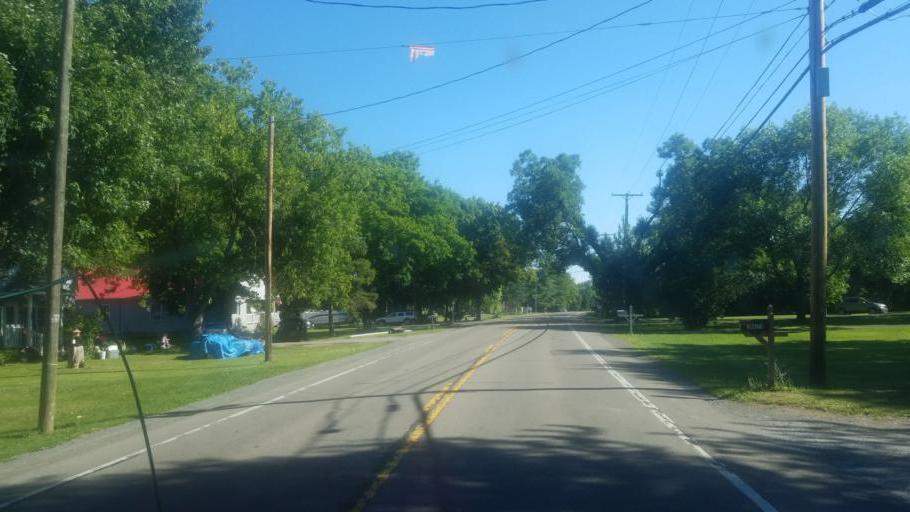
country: US
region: New York
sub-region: Ontario County
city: Canandaigua
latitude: 42.8511
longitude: -77.2550
